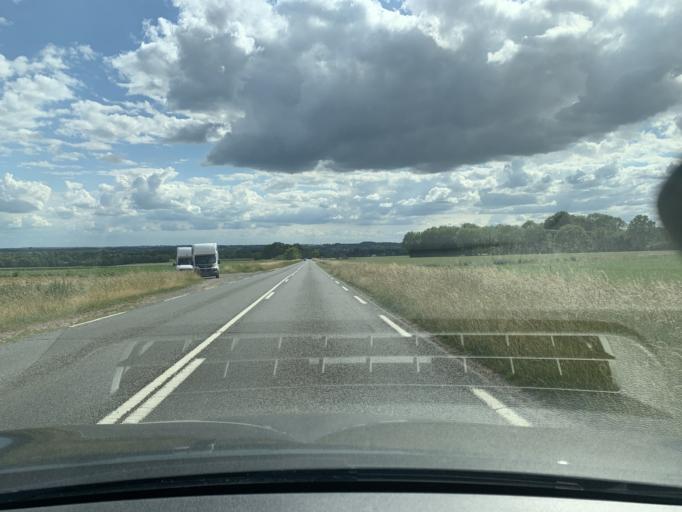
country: FR
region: Picardie
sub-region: Departement de la Somme
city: Peronne
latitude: 49.9477
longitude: 2.9562
